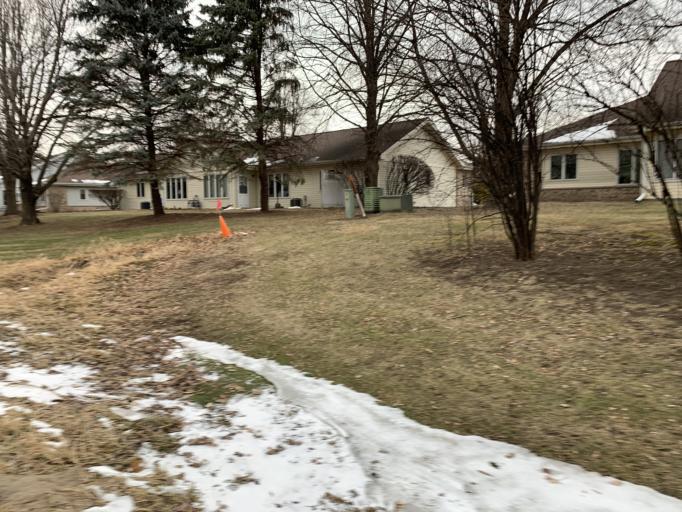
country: US
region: Wisconsin
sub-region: Dane County
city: Middleton
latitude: 43.0759
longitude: -89.5101
